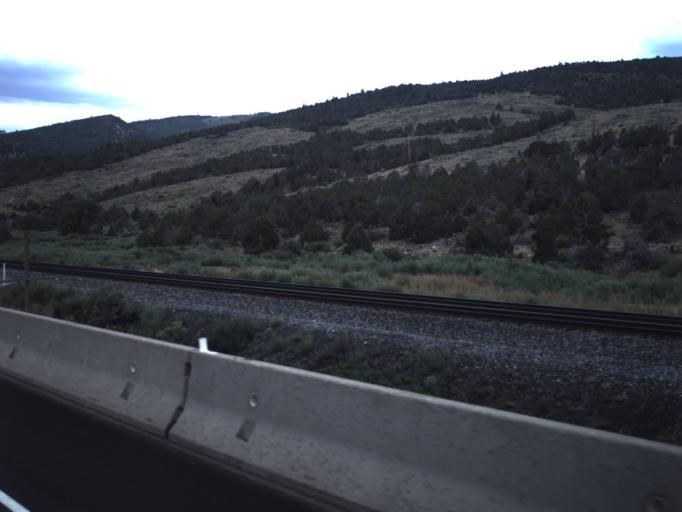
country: US
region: Utah
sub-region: Utah County
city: Mapleton
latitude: 39.9544
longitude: -111.2962
